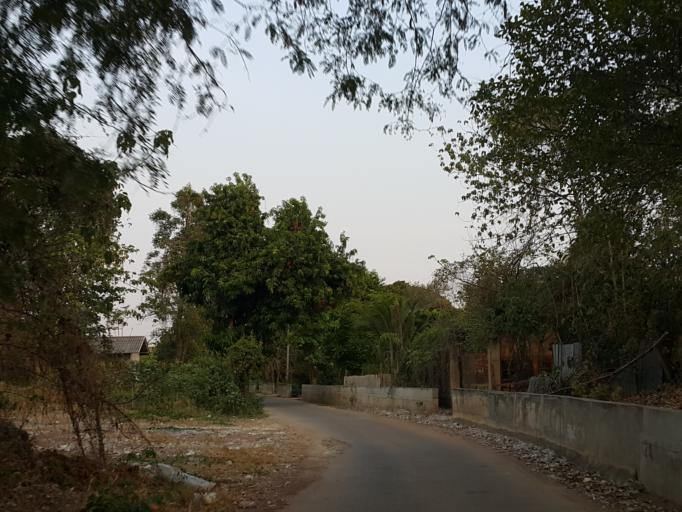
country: TH
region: Sukhothai
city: Sawankhalok
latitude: 17.2971
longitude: 99.8316
